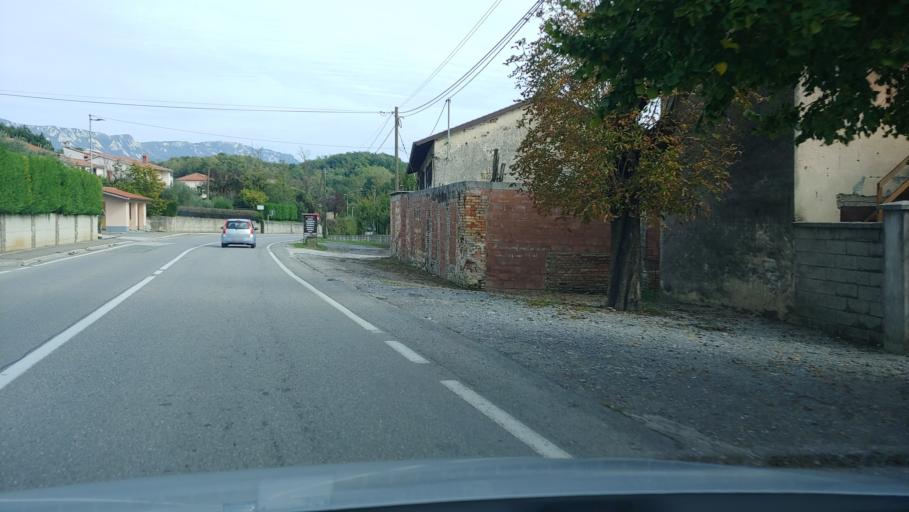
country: SI
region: Ajdovscina
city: Lokavec
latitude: 45.8850
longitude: 13.8385
